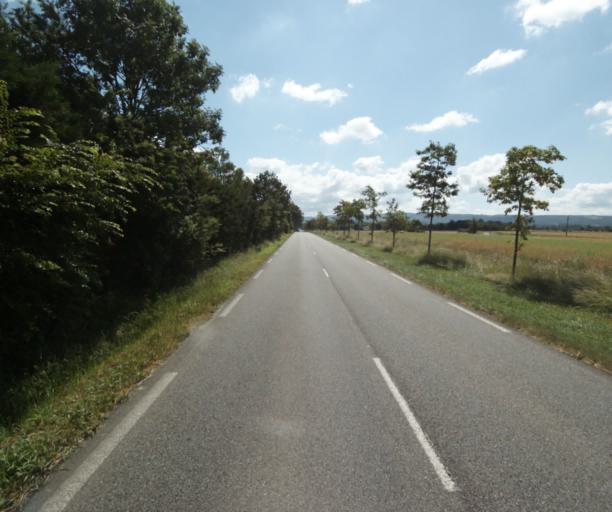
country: FR
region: Midi-Pyrenees
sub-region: Departement de la Haute-Garonne
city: Saint-Felix-Lauragais
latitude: 43.4472
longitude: 1.9341
